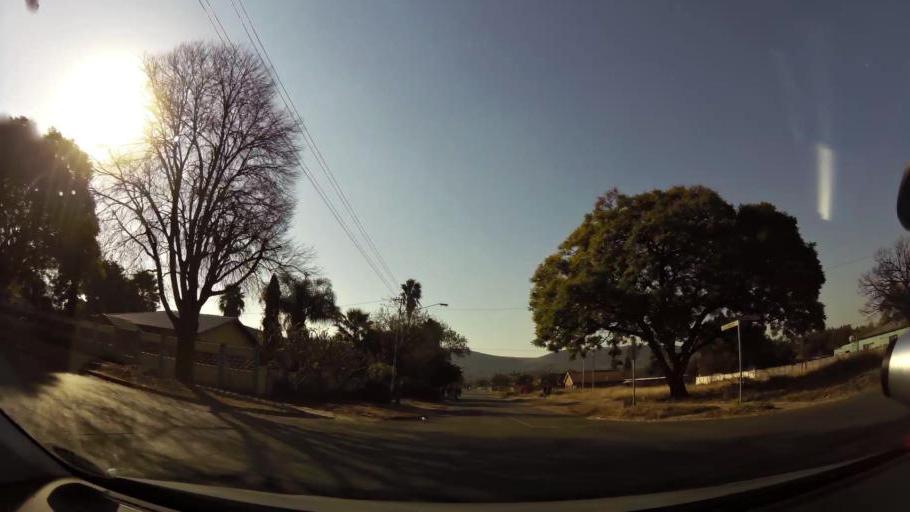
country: ZA
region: Gauteng
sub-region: City of Tshwane Metropolitan Municipality
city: Pretoria
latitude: -25.7144
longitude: 28.1539
